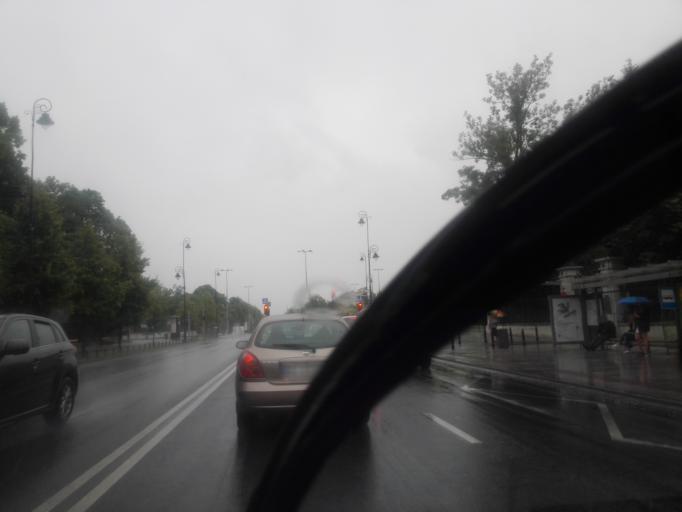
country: PL
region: Masovian Voivodeship
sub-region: Warszawa
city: Srodmiescie
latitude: 52.2211
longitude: 21.0247
